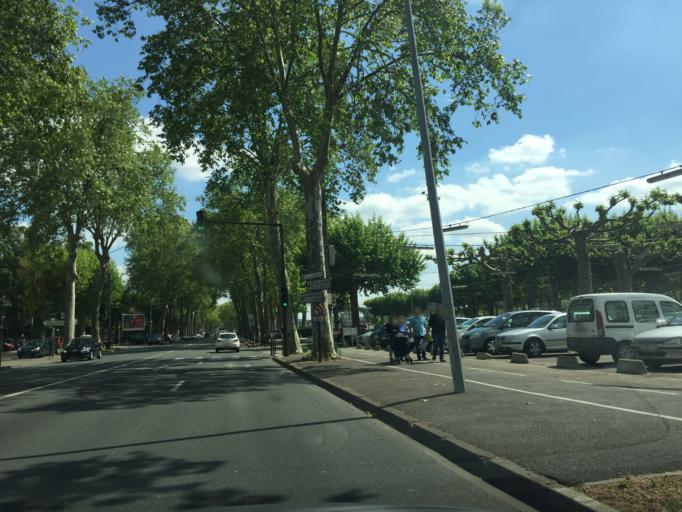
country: FR
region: Aquitaine
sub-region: Departement du Lot-et-Garonne
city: Le Passage
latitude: 44.2030
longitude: 0.6118
